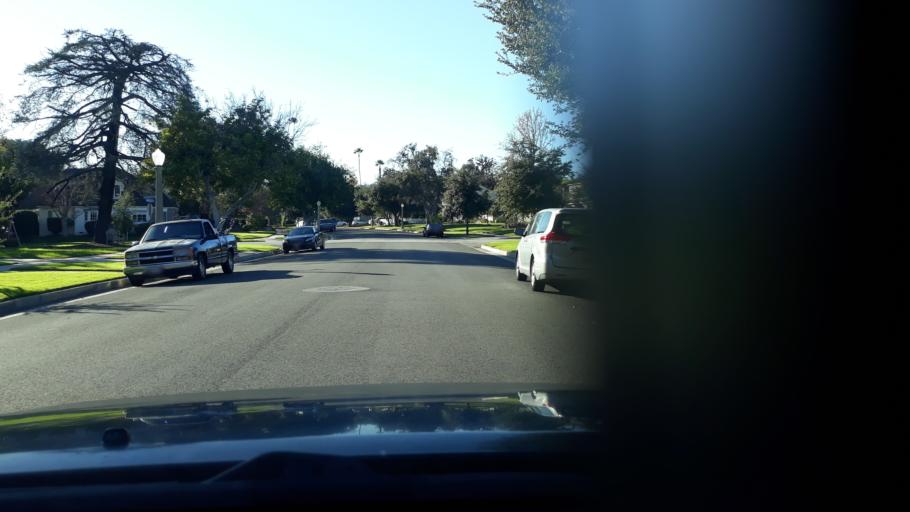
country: US
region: California
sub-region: Los Angeles County
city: San Marino
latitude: 34.1207
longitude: -118.1008
